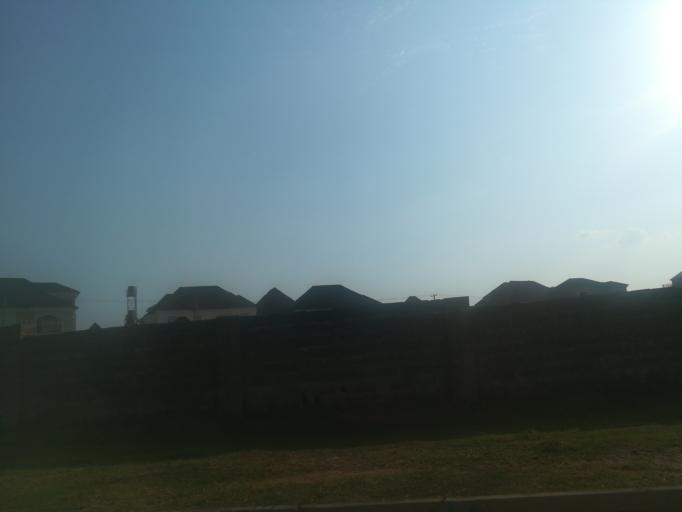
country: NG
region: Abuja Federal Capital Territory
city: Abuja
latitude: 9.0474
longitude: 7.4402
